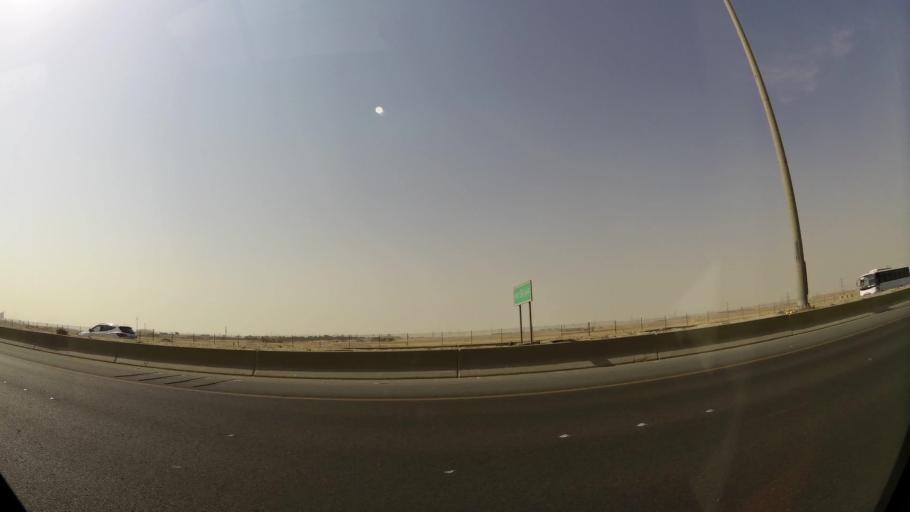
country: KW
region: Al Ahmadi
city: Al Fahahil
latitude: 29.0306
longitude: 48.1220
